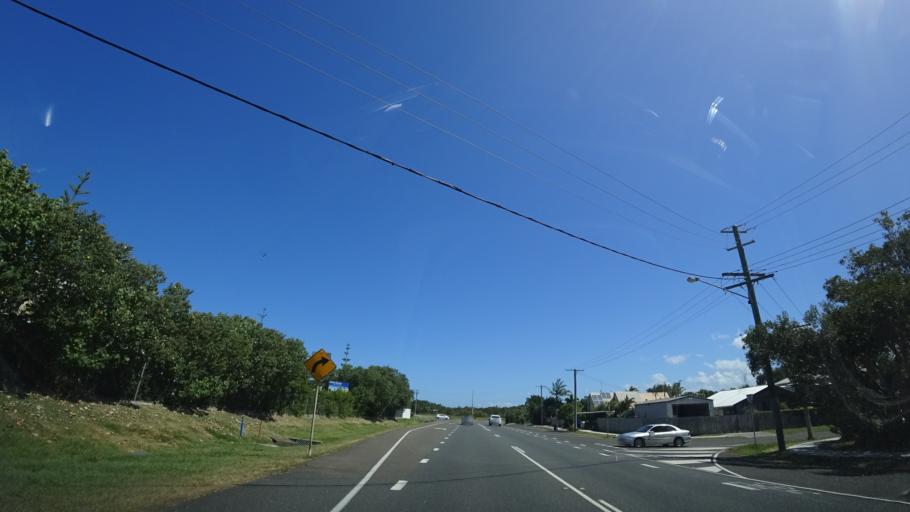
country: AU
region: Queensland
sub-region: Sunshine Coast
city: Coolum Beach
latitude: -26.6056
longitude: 153.0966
